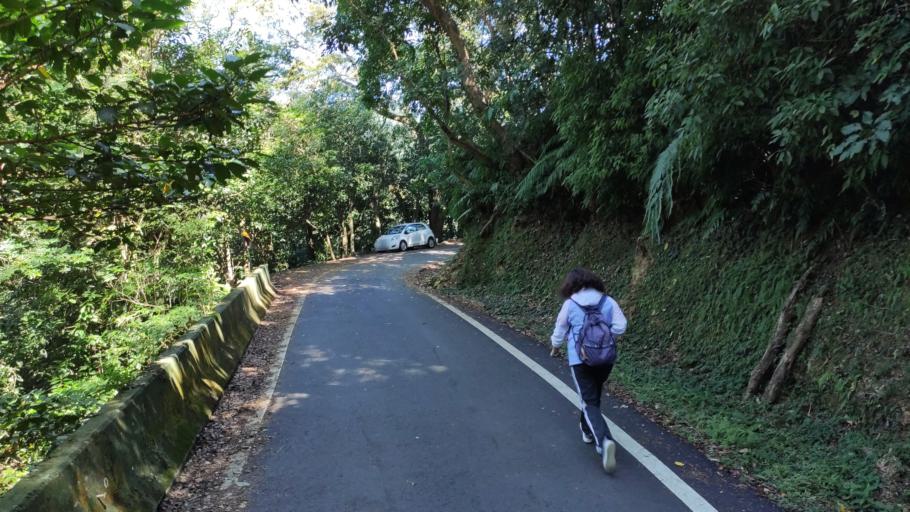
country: TW
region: Taiwan
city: Daxi
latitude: 24.8366
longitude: 121.3045
